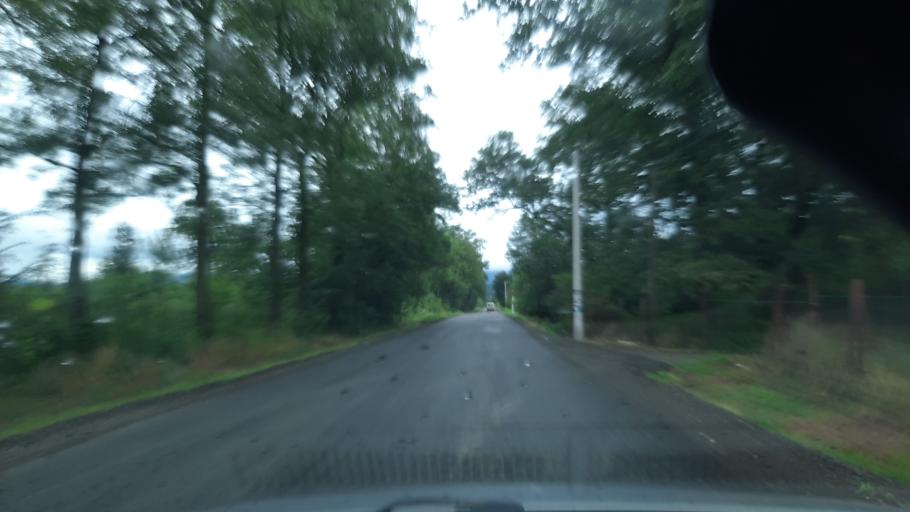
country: RS
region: Central Serbia
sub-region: Raski Okrug
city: Kraljevo
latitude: 43.7170
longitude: 20.8116
